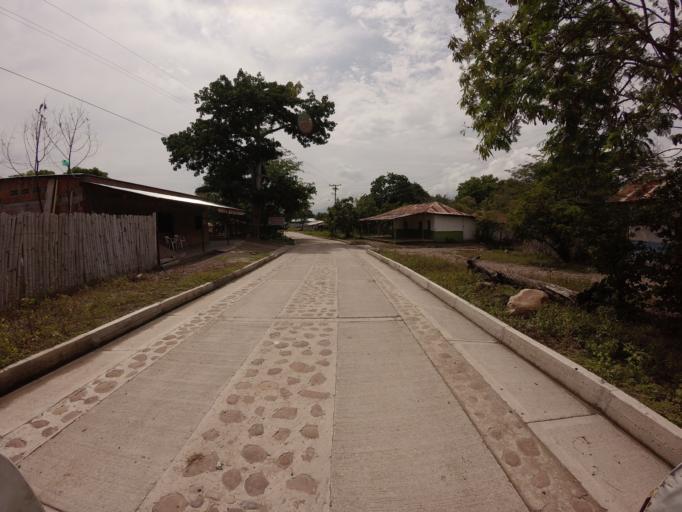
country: CO
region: Tolima
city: Natagaima
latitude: 3.4585
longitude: -75.1425
